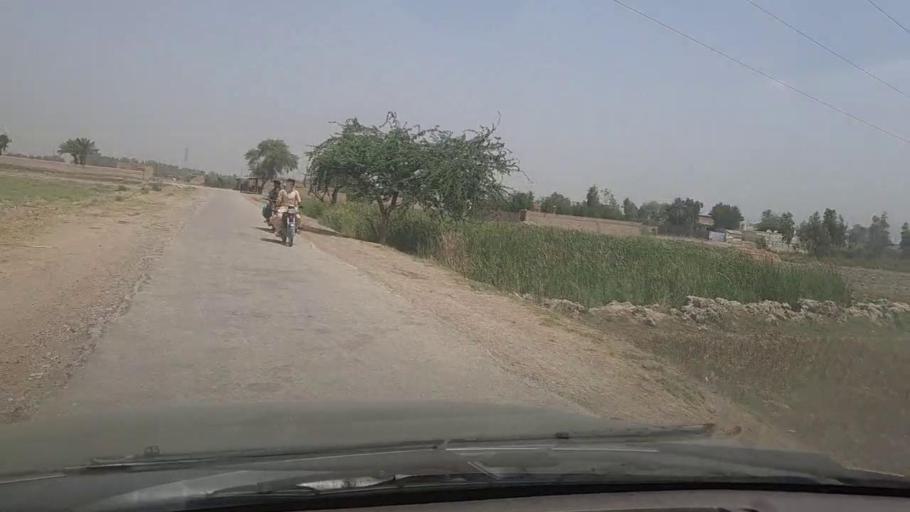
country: PK
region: Sindh
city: Madeji
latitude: 27.8241
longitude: 68.3951
